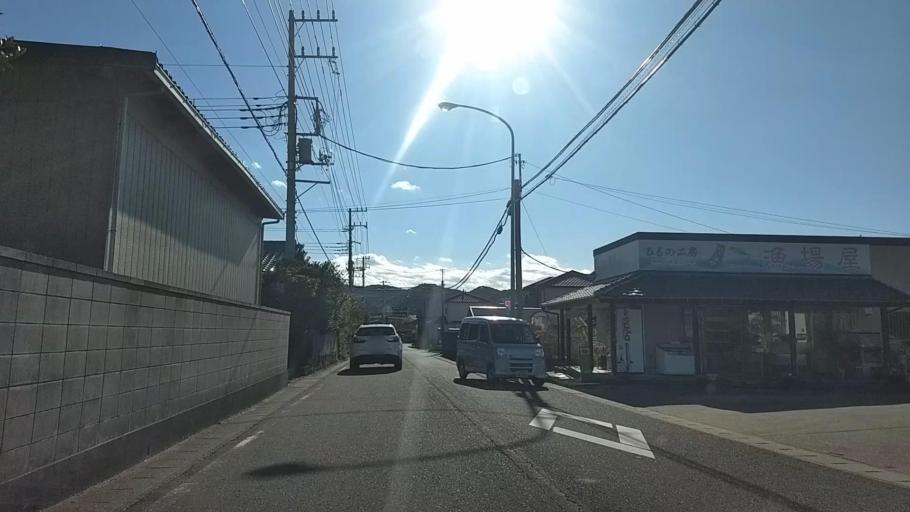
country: JP
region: Chiba
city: Futtsu
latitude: 35.1442
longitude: 139.8346
